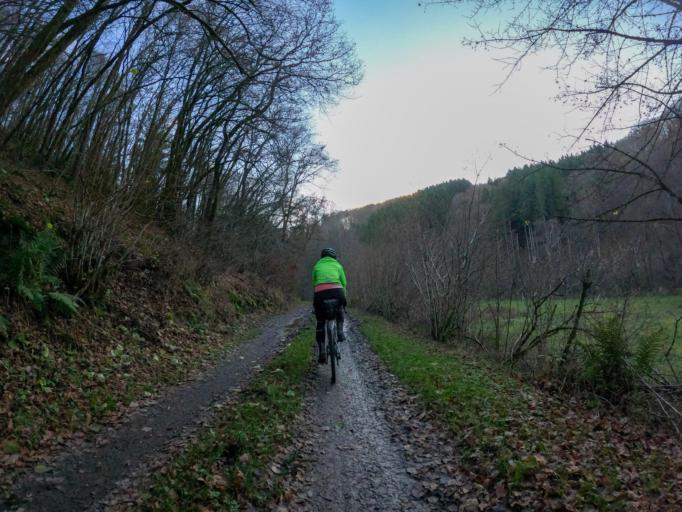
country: LU
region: Diekirch
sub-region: Canton de Wiltz
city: Bavigne
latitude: 49.9431
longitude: 5.8334
